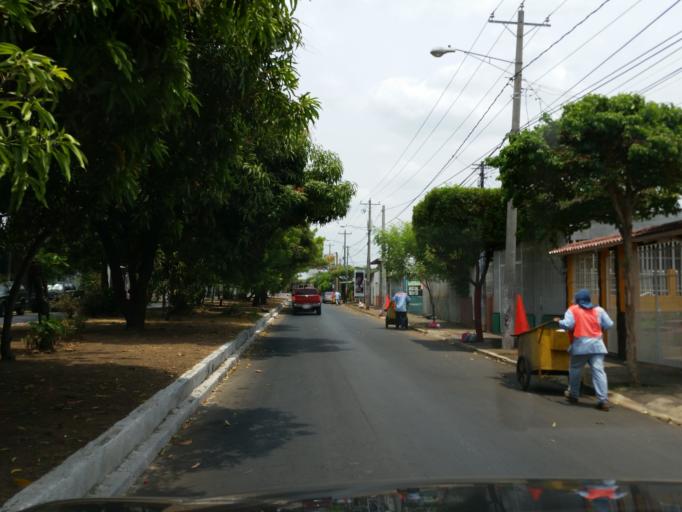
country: NI
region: Managua
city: Managua
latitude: 12.1410
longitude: -86.2335
